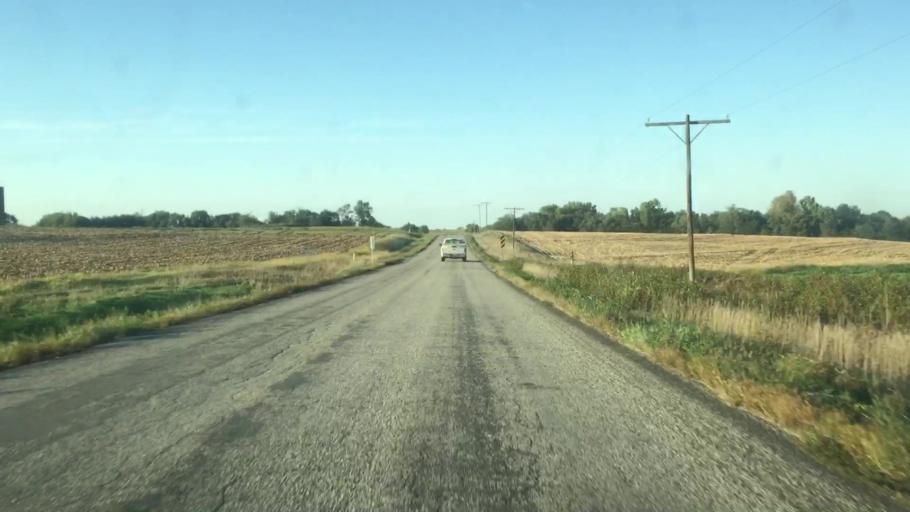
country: US
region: Kansas
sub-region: Brown County
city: Horton
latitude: 39.5553
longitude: -95.4021
